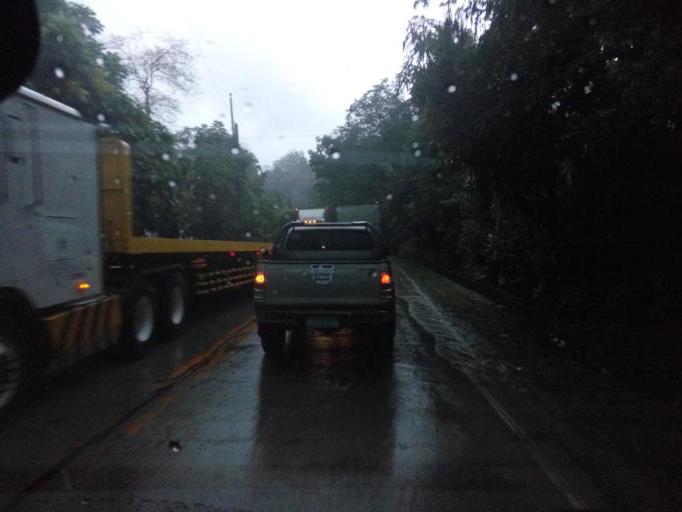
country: PH
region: Cagayan Valley
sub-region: Province of Nueva Vizcaya
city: Santa Fe
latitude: 16.1564
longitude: 120.9378
